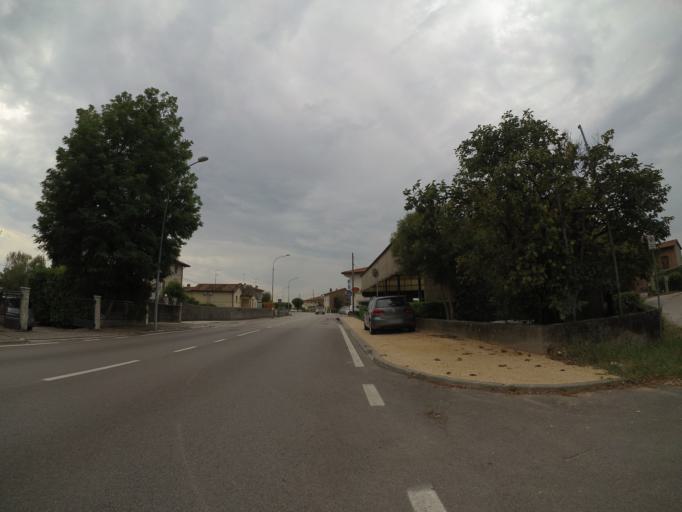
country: IT
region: Friuli Venezia Giulia
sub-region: Provincia di Udine
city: Codroipo
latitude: 45.9541
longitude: 12.9734
